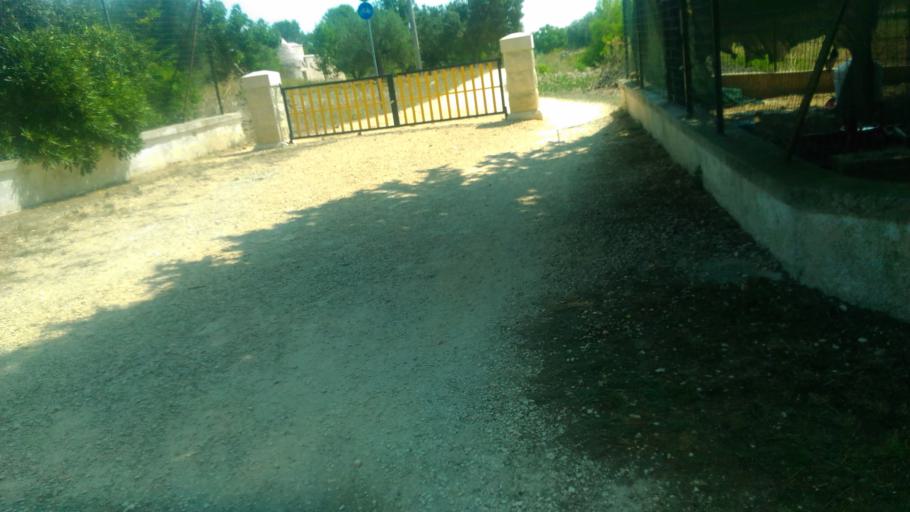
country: IT
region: Apulia
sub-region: Provincia di Brindisi
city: Cisternino
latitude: 40.7278
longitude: 17.3932
